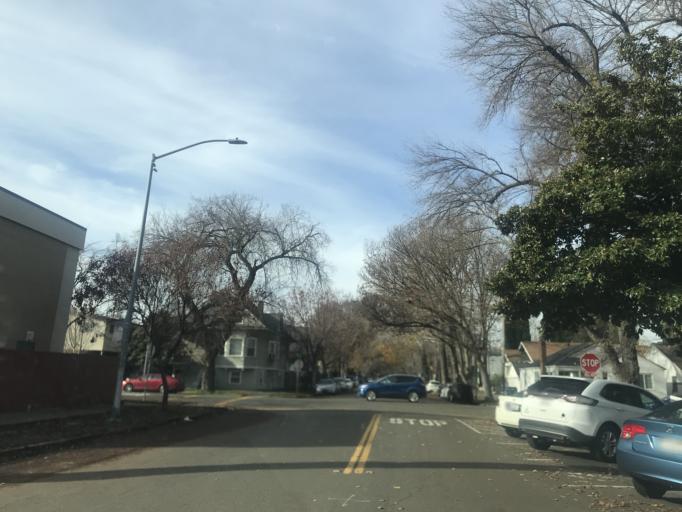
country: US
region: California
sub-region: Sacramento County
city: Sacramento
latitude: 38.5678
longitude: -121.4969
